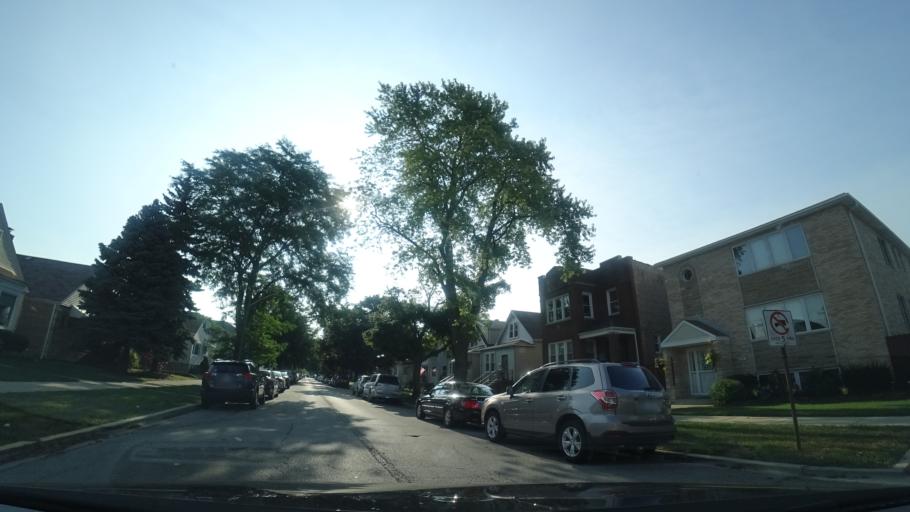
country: US
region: Illinois
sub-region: Cook County
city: Harwood Heights
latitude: 41.9668
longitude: -87.7772
